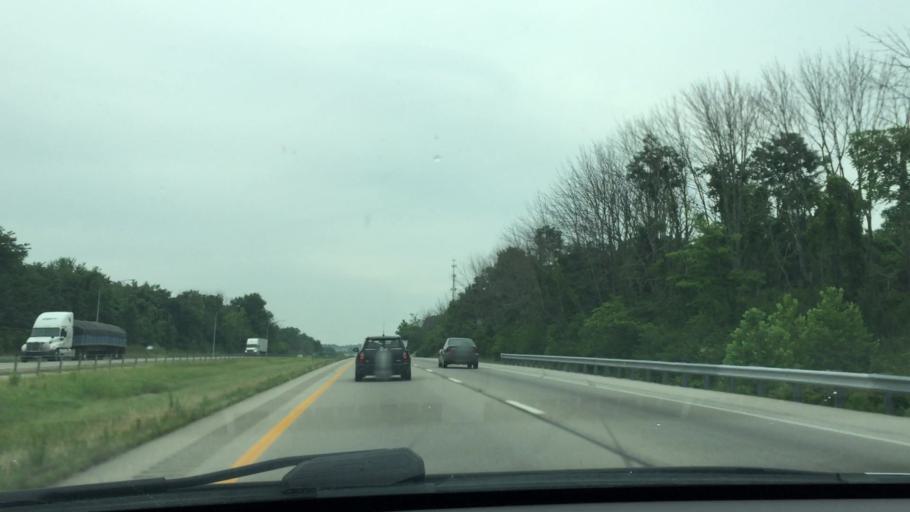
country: US
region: Kentucky
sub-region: Boone County
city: Walton
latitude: 38.8665
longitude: -84.6435
